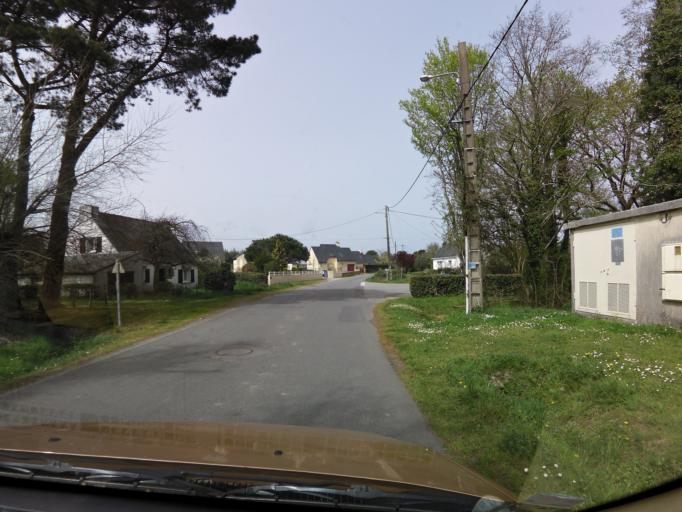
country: FR
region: Brittany
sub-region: Departement du Morbihan
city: Sene
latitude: 47.5759
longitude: -2.7106
